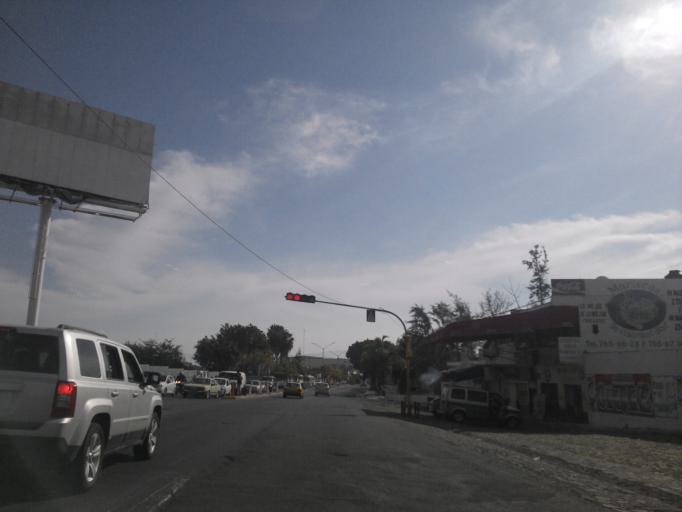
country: MX
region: Jalisco
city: Chapala
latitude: 20.2981
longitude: -103.1904
